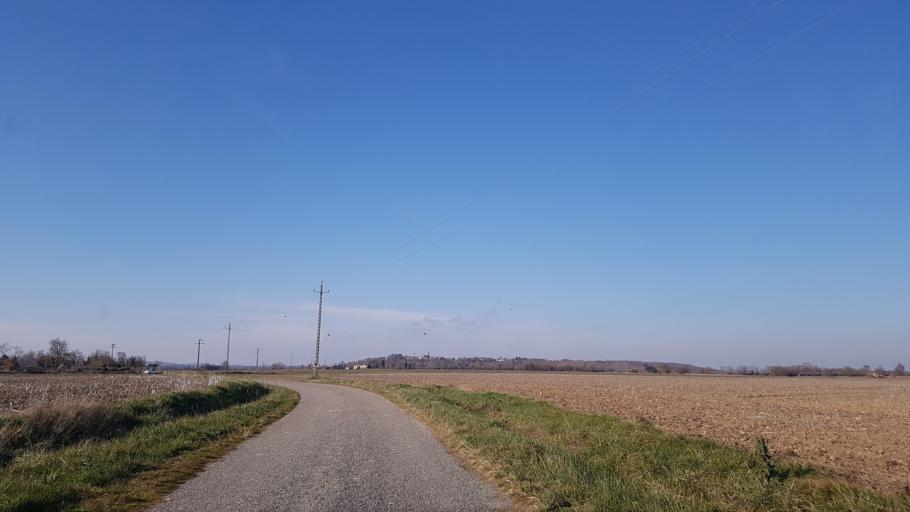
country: FR
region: Midi-Pyrenees
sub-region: Departement de l'Ariege
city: La Tour-du-Crieu
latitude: 43.1726
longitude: 1.6629
